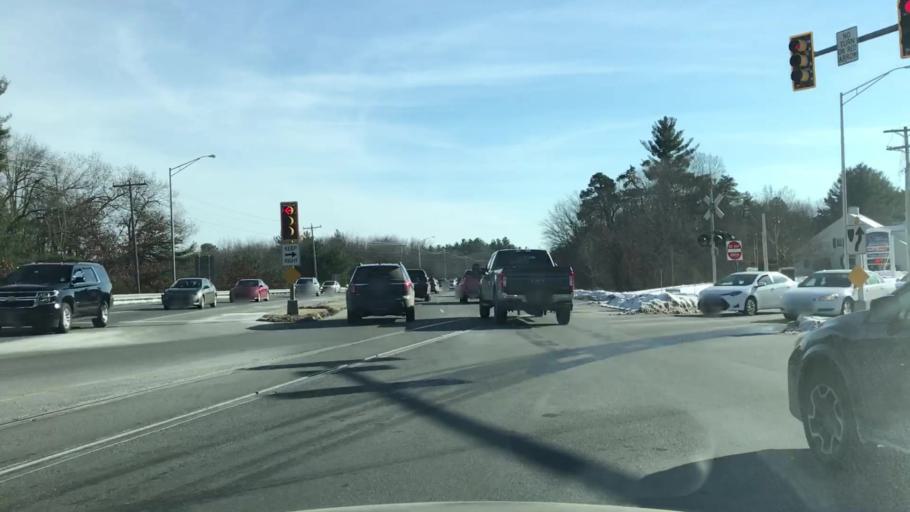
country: US
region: New Hampshire
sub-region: Hillsborough County
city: Milford
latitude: 42.8221
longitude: -71.6063
